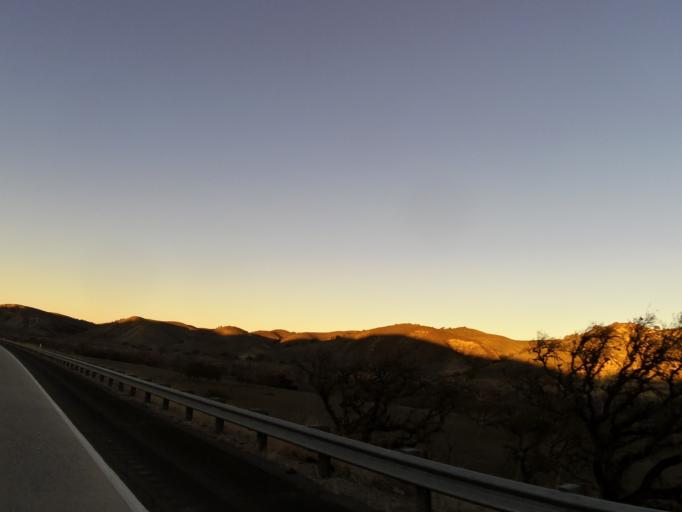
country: US
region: California
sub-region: San Luis Obispo County
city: Lake Nacimiento
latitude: 35.8979
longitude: -120.8412
